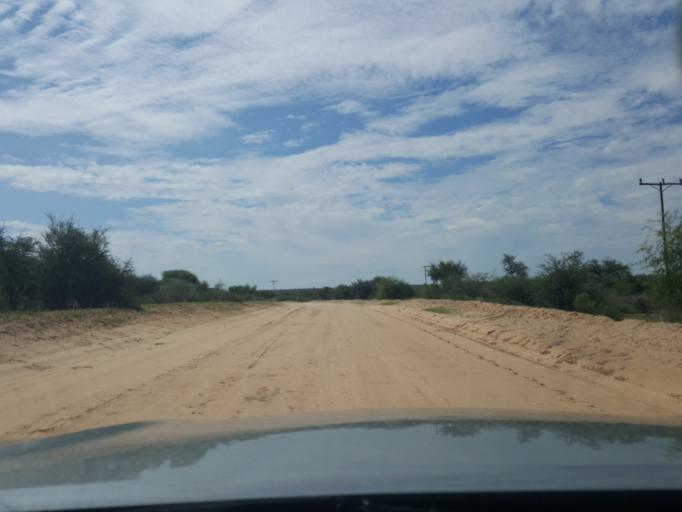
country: BW
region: Kweneng
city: Letlhakeng
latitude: -24.0574
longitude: 25.0309
